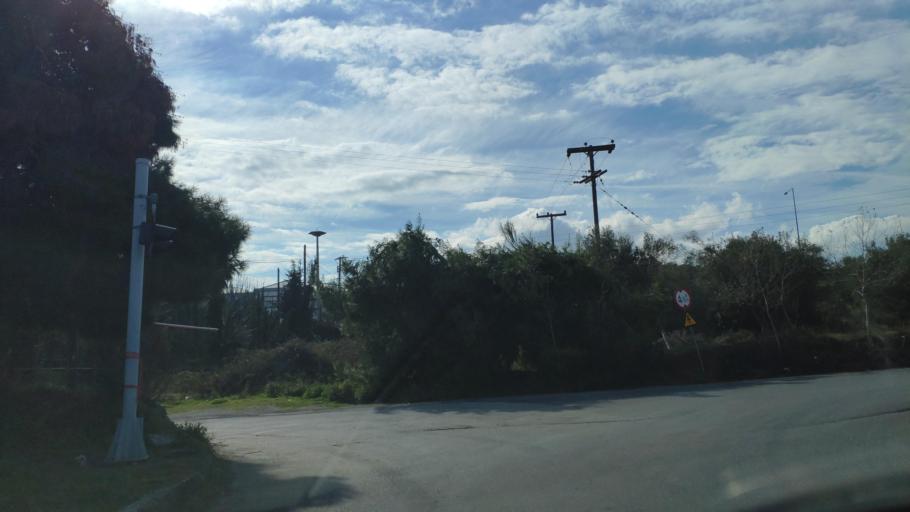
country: GR
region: Central Greece
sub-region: Nomos Evvoias
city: Vathi
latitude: 38.4165
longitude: 23.5916
